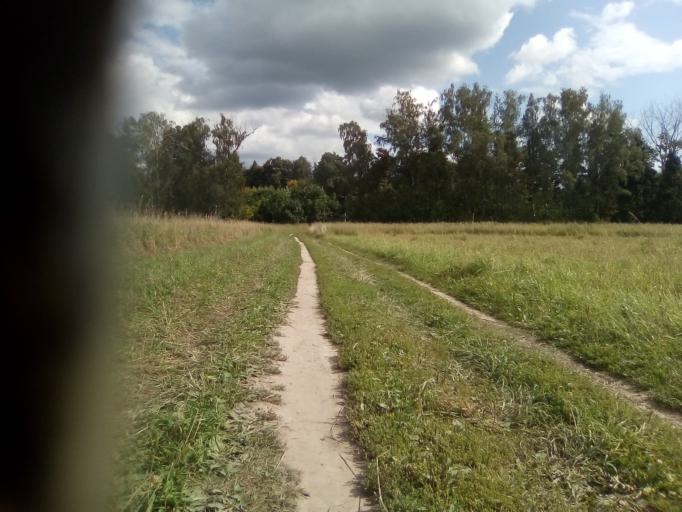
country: RU
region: Moskovskaya
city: Zhavoronki
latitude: 55.6501
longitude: 37.1467
